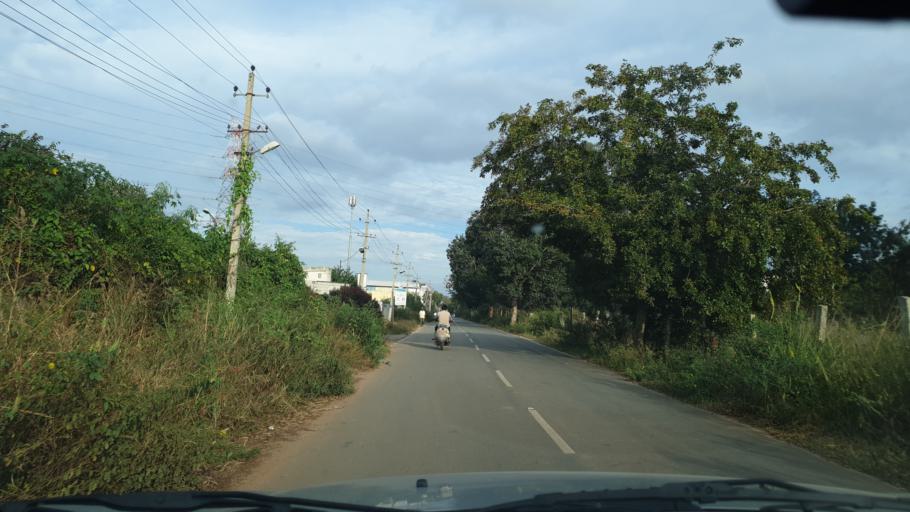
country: IN
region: Karnataka
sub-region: Bangalore Rural
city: Devanhalli
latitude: 13.1890
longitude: 77.6361
